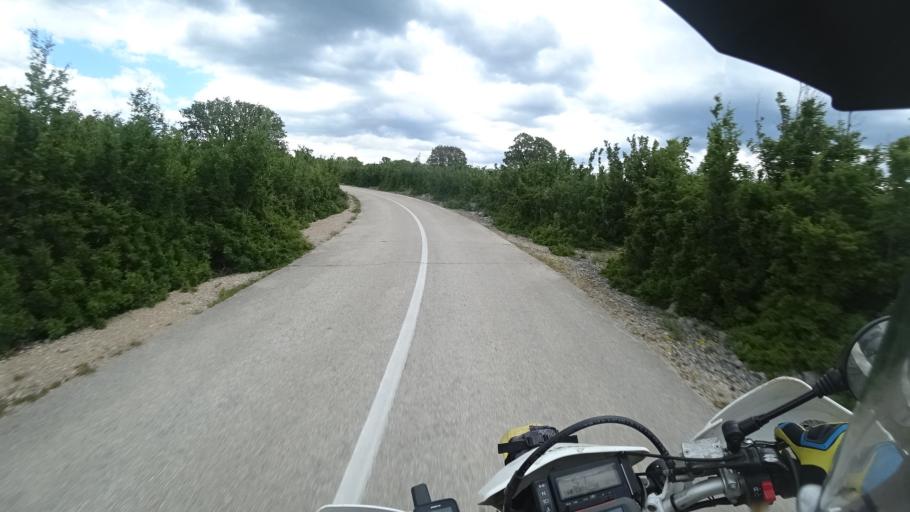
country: HR
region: Zadarska
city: Gracac
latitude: 44.1975
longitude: 15.8740
